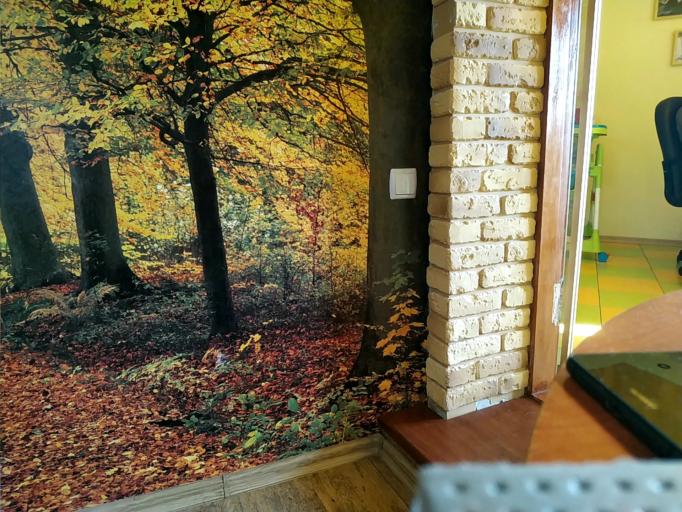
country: RU
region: Tverskaya
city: Zubtsov
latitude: 56.2062
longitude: 34.5447
